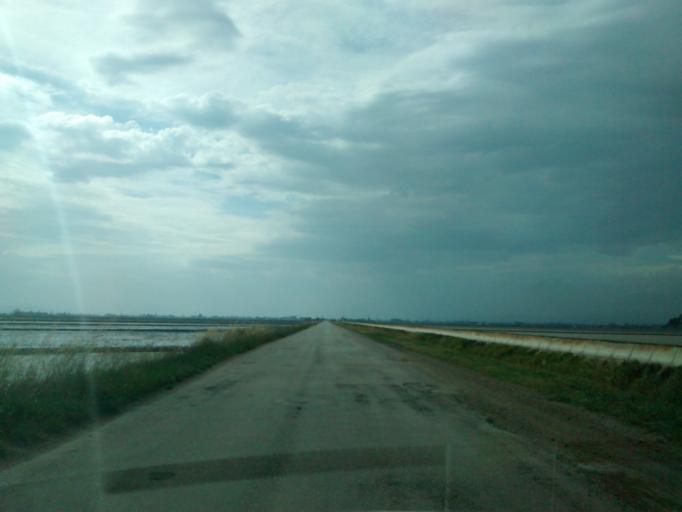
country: ES
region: Catalonia
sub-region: Provincia de Tarragona
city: Deltebre
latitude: 40.6940
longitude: 0.7689
